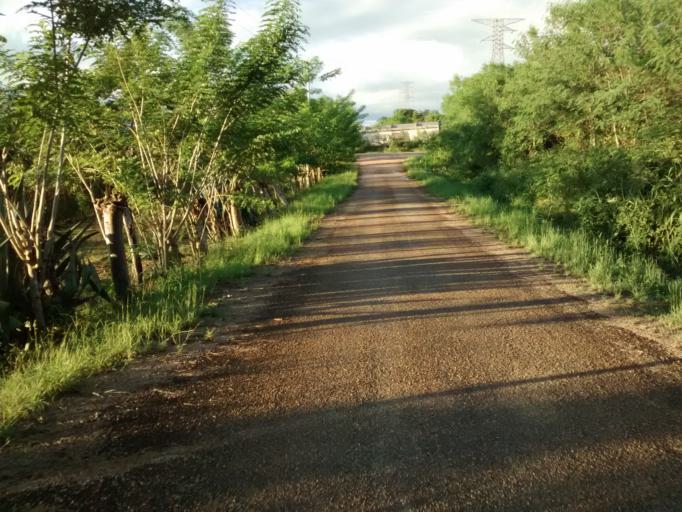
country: MX
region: Yucatan
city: Valladolid
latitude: 20.7242
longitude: -88.2047
